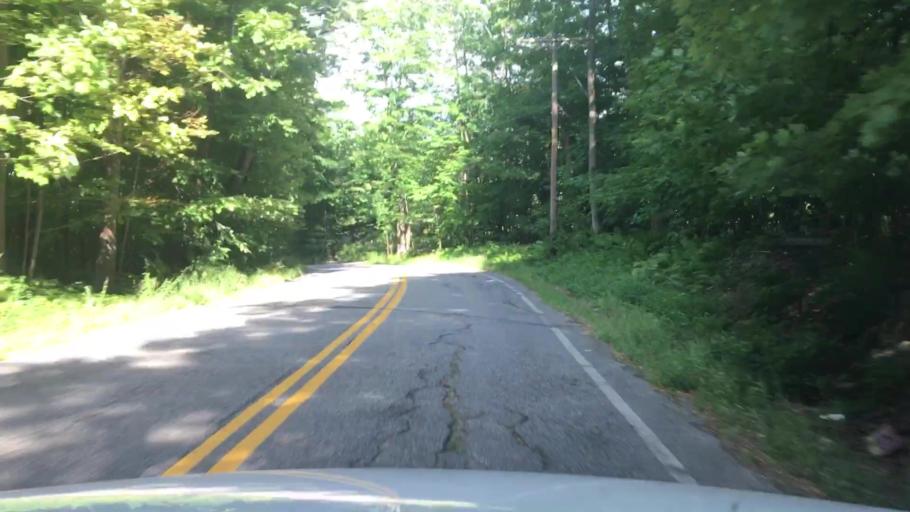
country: US
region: New Hampshire
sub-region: Belknap County
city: Gilford
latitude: 43.5673
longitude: -71.4129
